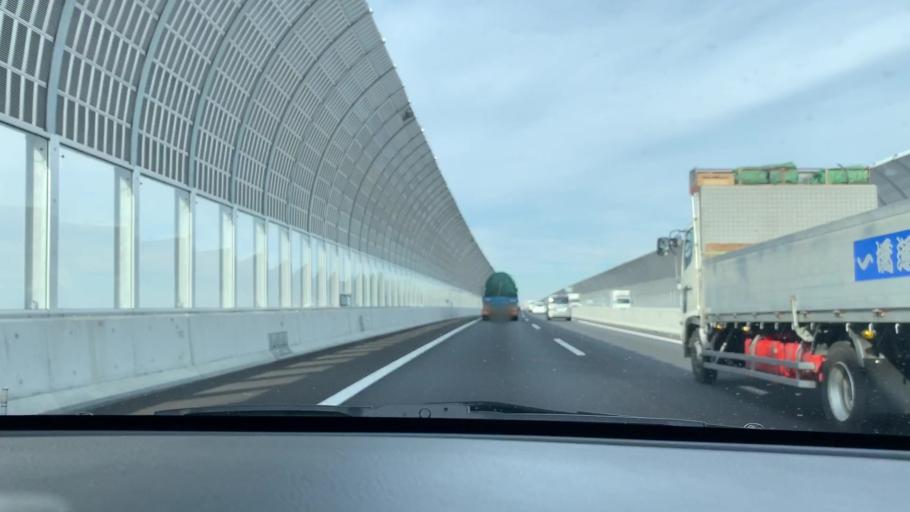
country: JP
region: Chiba
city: Matsudo
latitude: 35.7926
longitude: 139.8792
